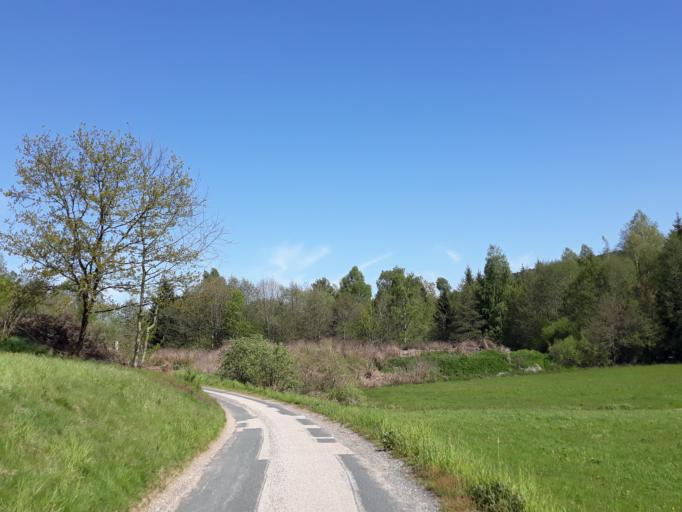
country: FR
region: Lorraine
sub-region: Departement des Vosges
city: Granges-sur-Vologne
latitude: 48.1375
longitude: 6.7906
